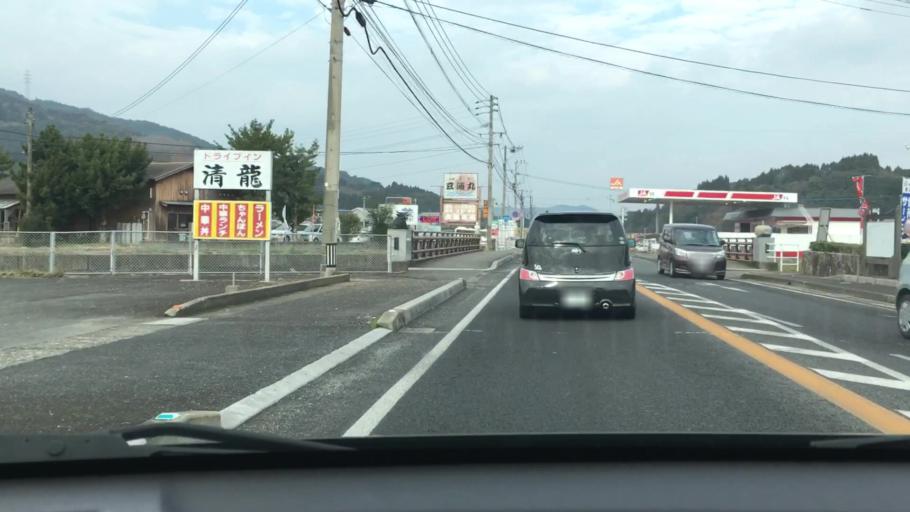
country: JP
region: Saga Prefecture
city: Imaricho-ko
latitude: 33.3140
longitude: 129.9286
